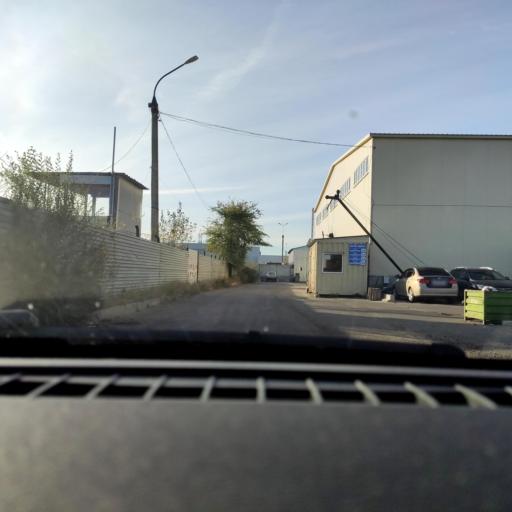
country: RU
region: Voronezj
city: Somovo
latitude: 51.6715
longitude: 39.2991
